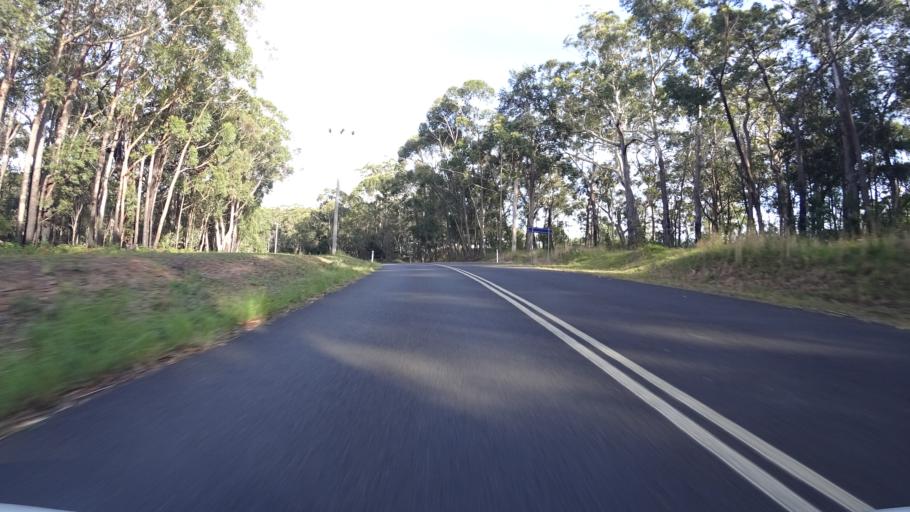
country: AU
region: New South Wales
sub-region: Shoalhaven Shire
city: Milton
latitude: -35.2609
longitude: 150.5066
